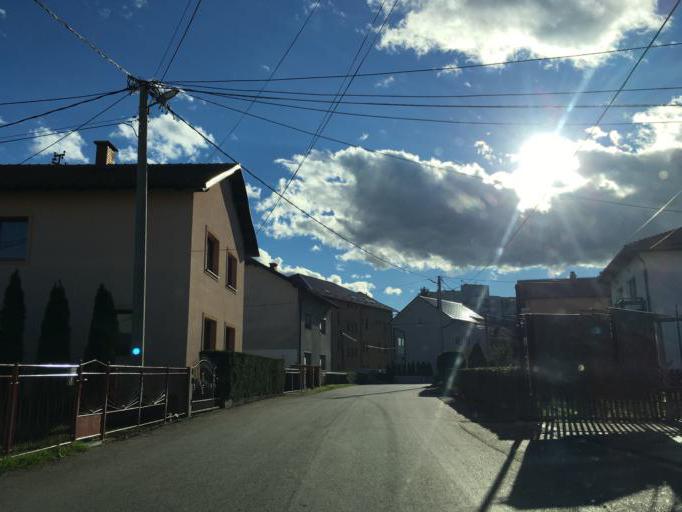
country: BA
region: Federation of Bosnia and Herzegovina
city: Bugojno
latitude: 44.0537
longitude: 17.4522
